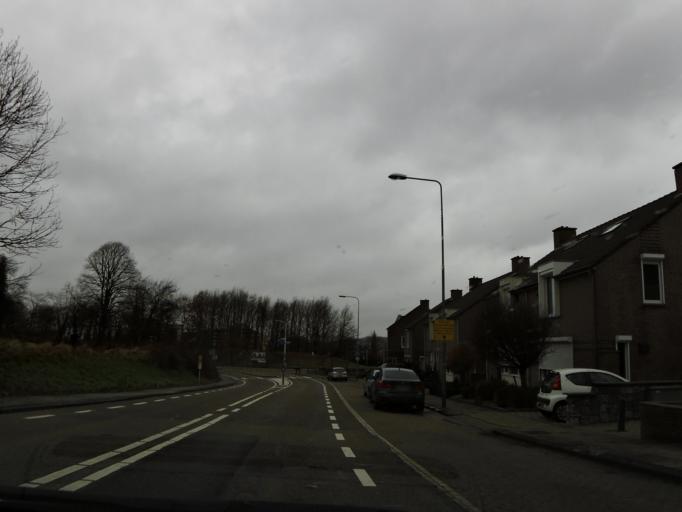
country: NL
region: Limburg
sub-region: Gemeente Vaals
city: Vaals
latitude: 50.7667
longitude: 6.0111
